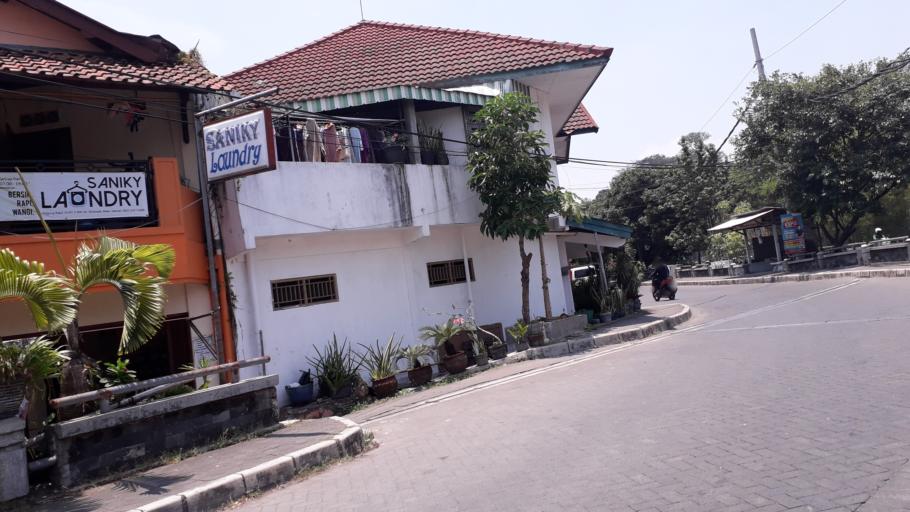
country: ID
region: Daerah Istimewa Yogyakarta
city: Yogyakarta
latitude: -7.7636
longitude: 110.3738
